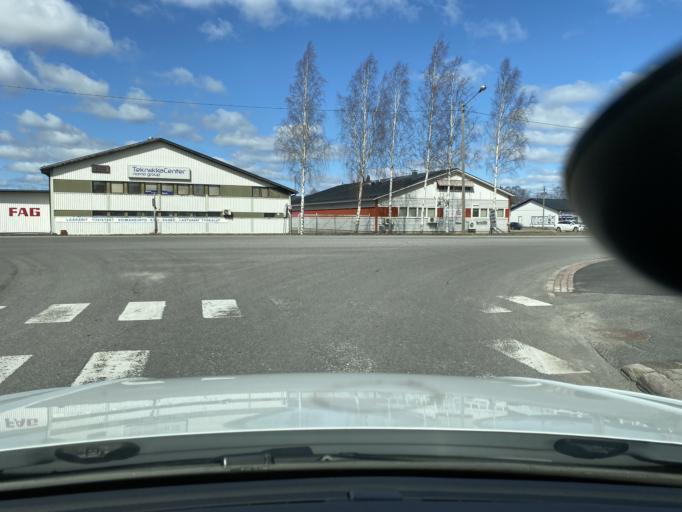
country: FI
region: Varsinais-Suomi
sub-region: Turku
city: Turku
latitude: 60.4836
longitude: 22.3118
